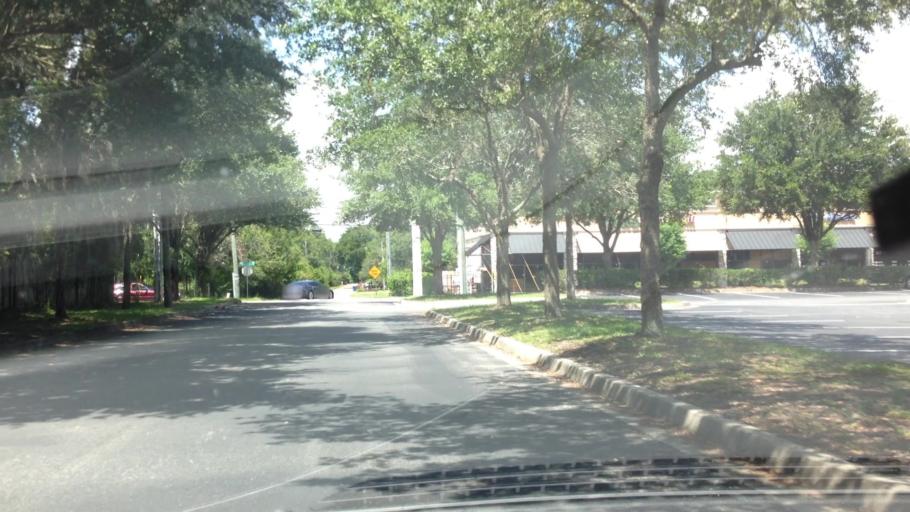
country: US
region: Florida
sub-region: Duval County
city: Jacksonville
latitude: 30.4591
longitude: -81.5783
